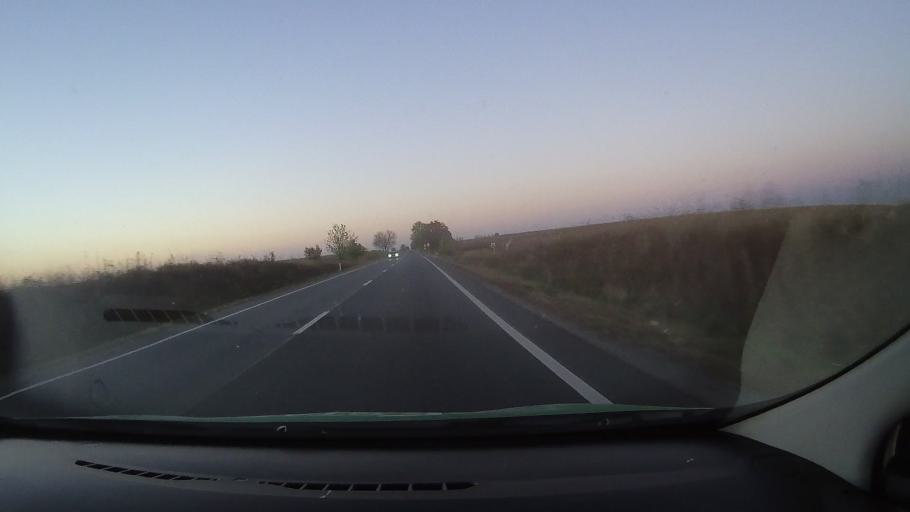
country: RO
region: Bihor
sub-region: Comuna Tarcea
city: Tarcea
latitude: 47.4702
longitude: 22.1654
